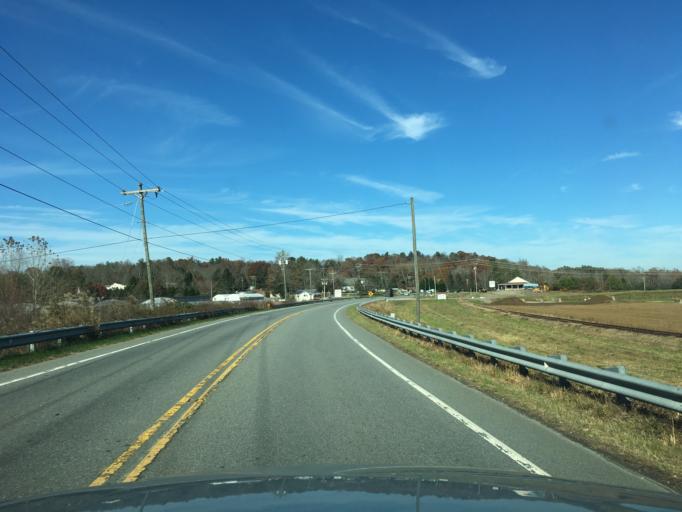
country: US
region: North Carolina
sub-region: Henderson County
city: Etowah
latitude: 35.2974
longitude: -82.6269
